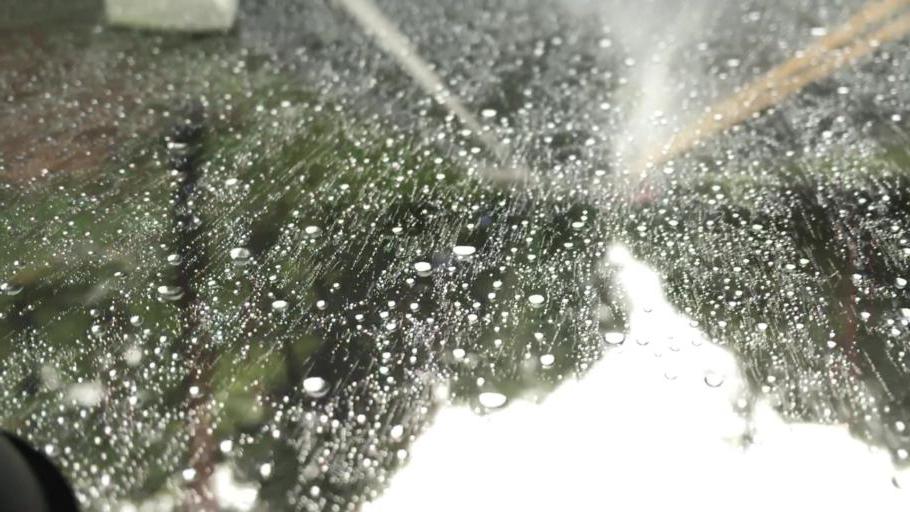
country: US
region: Pennsylvania
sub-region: Allegheny County
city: Allison Park
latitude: 40.5592
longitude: -79.9867
